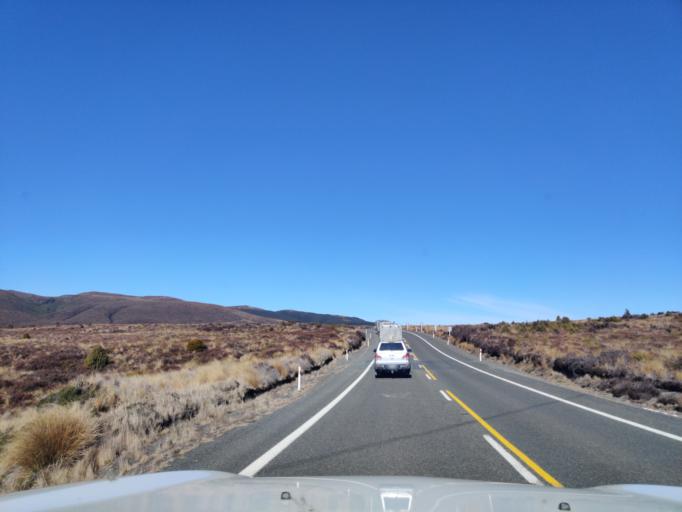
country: NZ
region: Manawatu-Wanganui
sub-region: Ruapehu District
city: Waiouru
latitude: -39.2716
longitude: 175.7384
